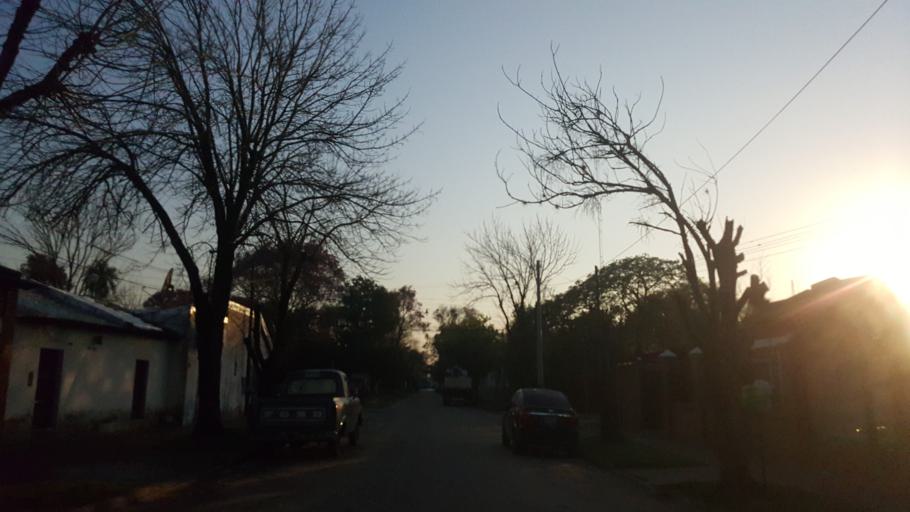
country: AR
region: Corrientes
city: Ituzaingo
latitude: -27.5894
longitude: -56.6881
